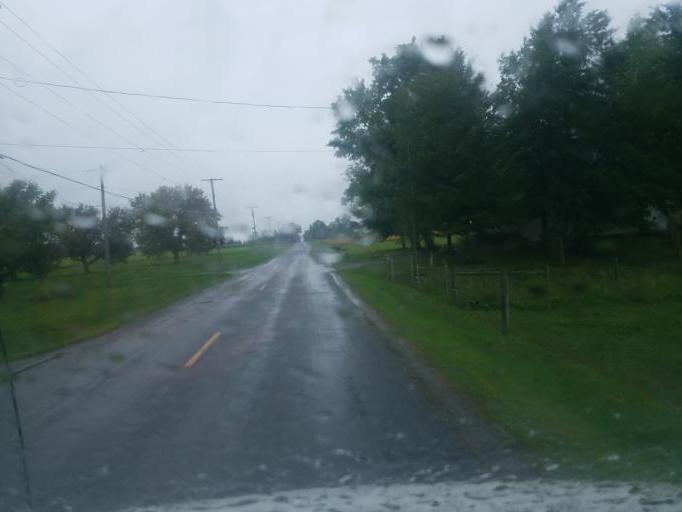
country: US
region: Ohio
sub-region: Medina County
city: Seville
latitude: 41.0194
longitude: -81.8326
